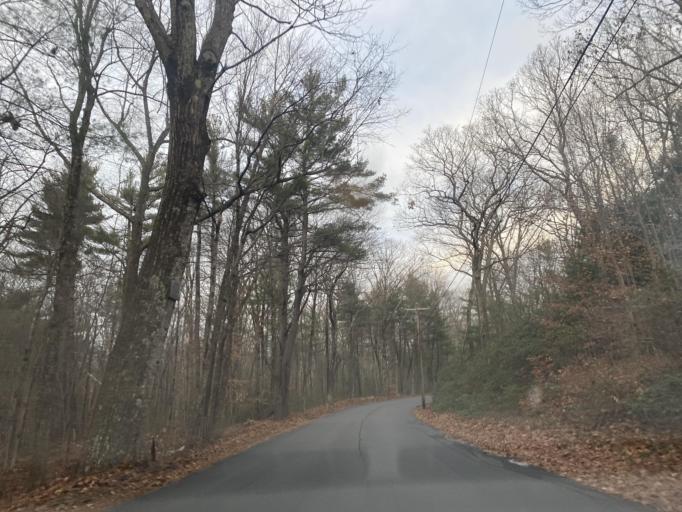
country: US
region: Massachusetts
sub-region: Worcester County
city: Leicester
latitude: 42.2656
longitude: -71.9460
